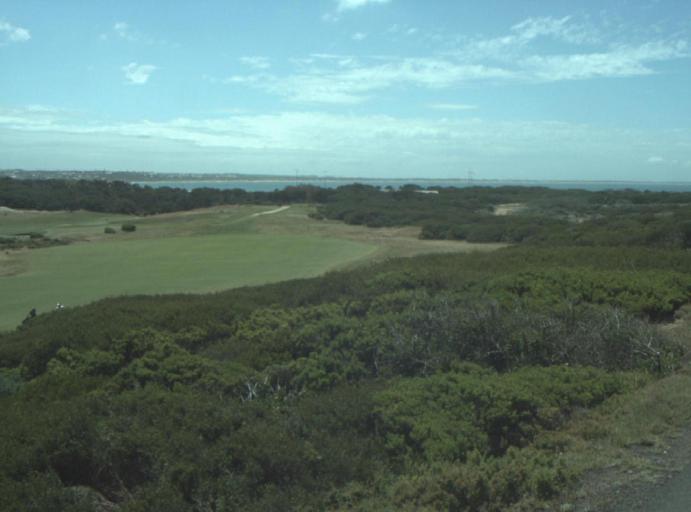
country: AU
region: Victoria
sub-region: Greater Geelong
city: Leopold
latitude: -38.2876
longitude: 144.4897
